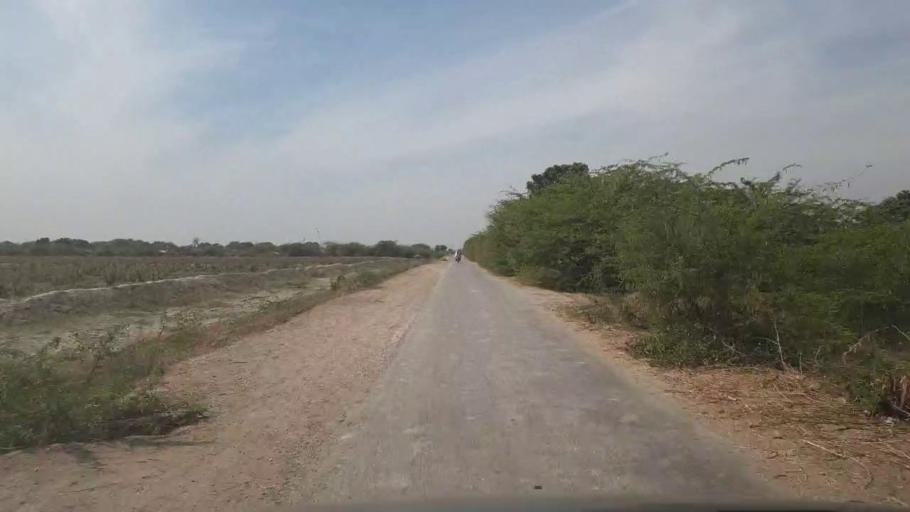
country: PK
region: Sindh
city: Kunri
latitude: 25.2120
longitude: 69.6071
